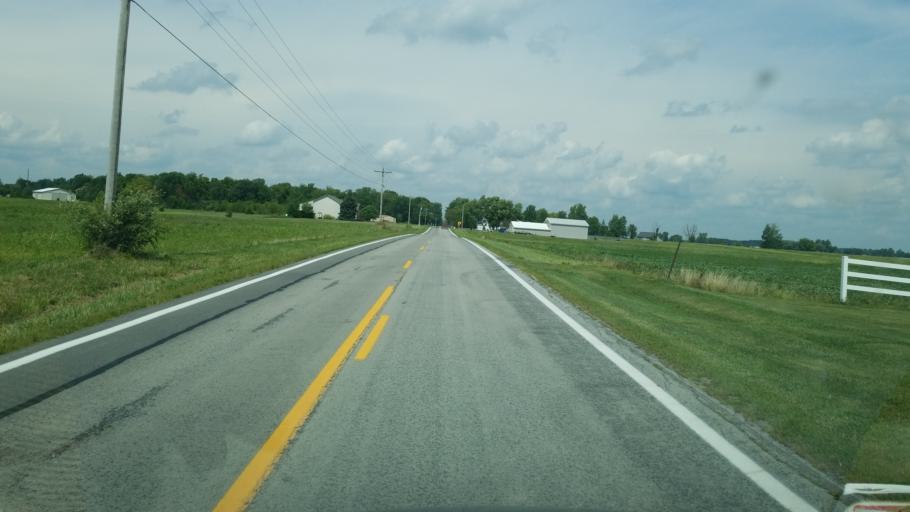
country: US
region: Ohio
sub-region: Hancock County
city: Findlay
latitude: 40.9805
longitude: -83.7275
